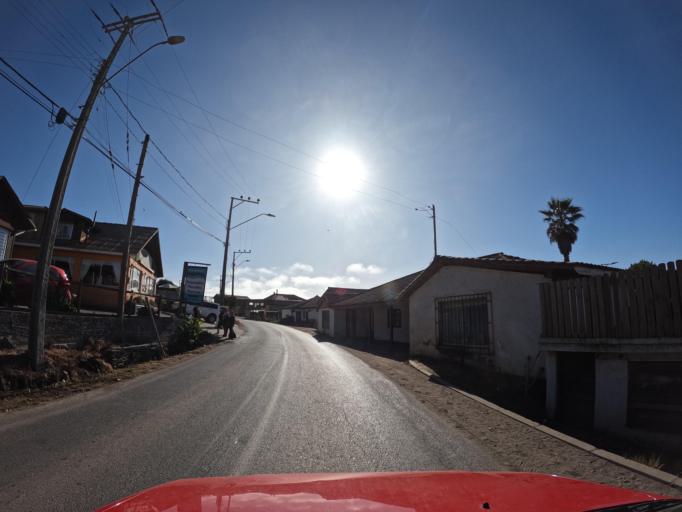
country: CL
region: Maule
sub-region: Provincia de Talca
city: Constitucion
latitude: -34.8858
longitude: -72.1672
